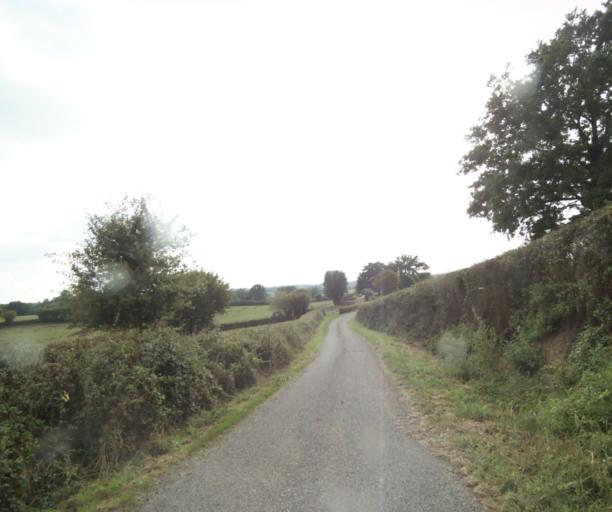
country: FR
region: Bourgogne
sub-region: Departement de Saone-et-Loire
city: Palinges
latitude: 46.5057
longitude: 4.2544
